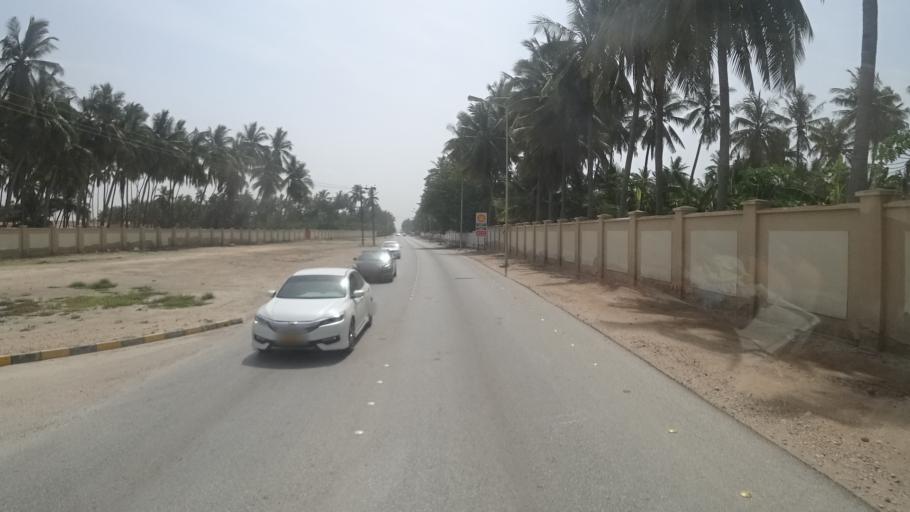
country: OM
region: Zufar
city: Salalah
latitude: 17.0143
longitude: 54.1503
